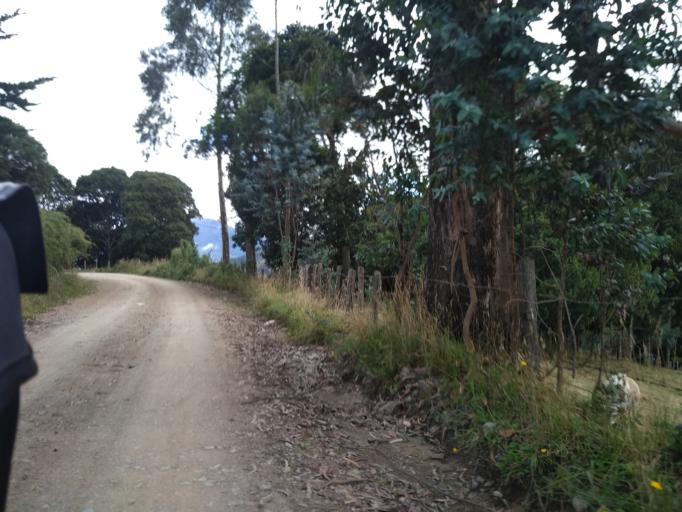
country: CO
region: Boyaca
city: Duitama
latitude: 5.9414
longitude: -73.1254
